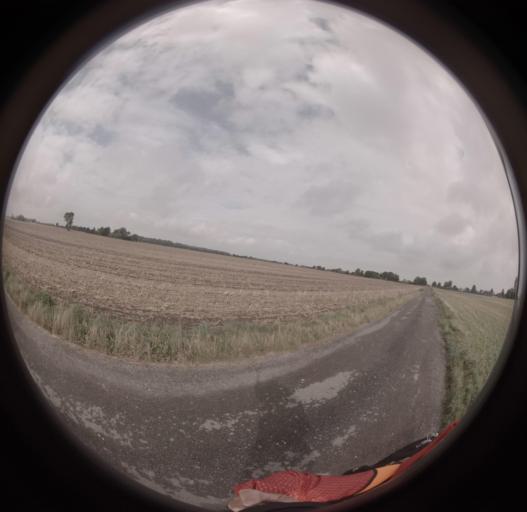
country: DK
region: South Denmark
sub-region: Nordfyns Kommune
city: Otterup
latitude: 55.5968
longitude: 10.3788
